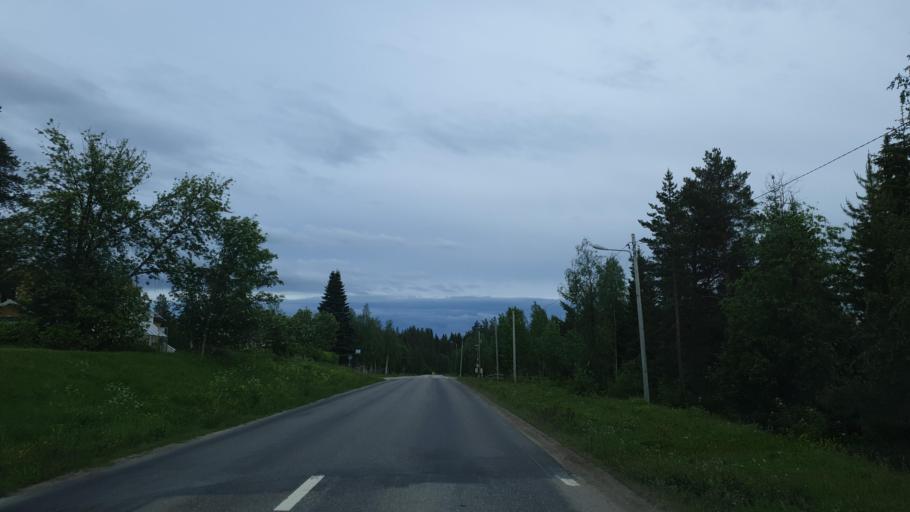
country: SE
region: Norrbotten
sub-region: Jokkmokks Kommun
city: Jokkmokk
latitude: 66.1532
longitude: 19.9826
